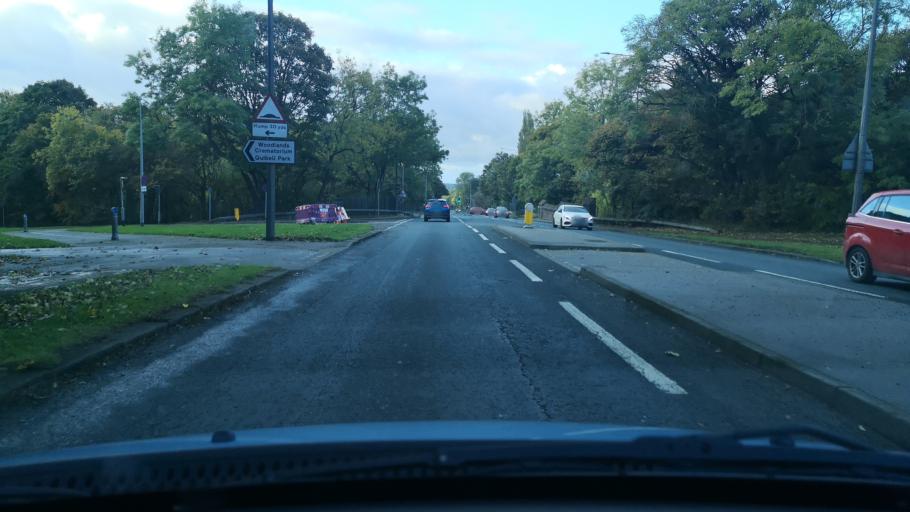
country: GB
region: England
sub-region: North Lincolnshire
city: Scunthorpe
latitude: 53.5842
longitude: -0.6723
